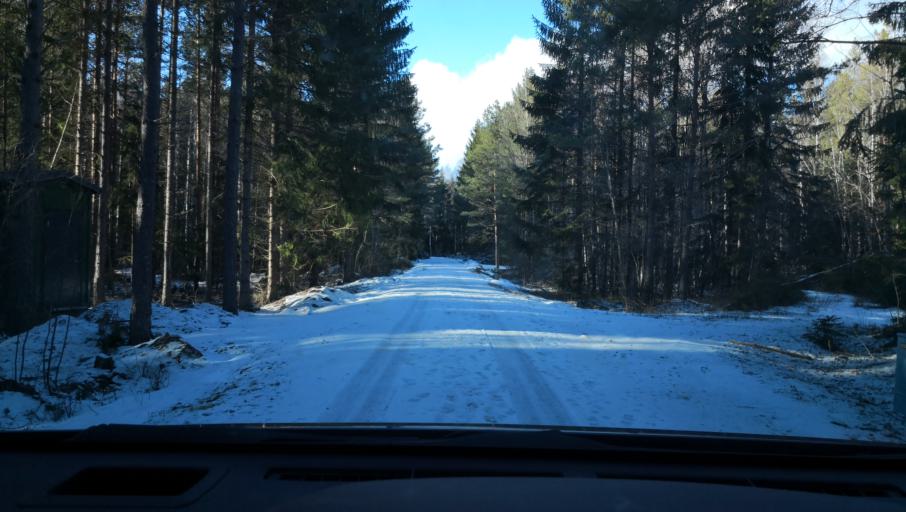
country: SE
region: Uppsala
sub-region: Enkopings Kommun
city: Hummelsta
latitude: 59.6246
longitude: 16.9312
